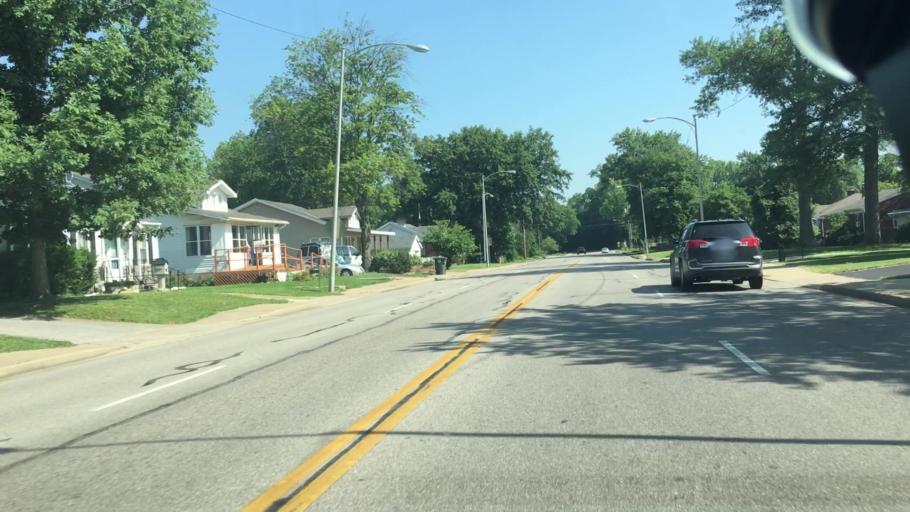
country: US
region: Indiana
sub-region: Vanderburgh County
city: Evansville
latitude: 37.9944
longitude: -87.5291
